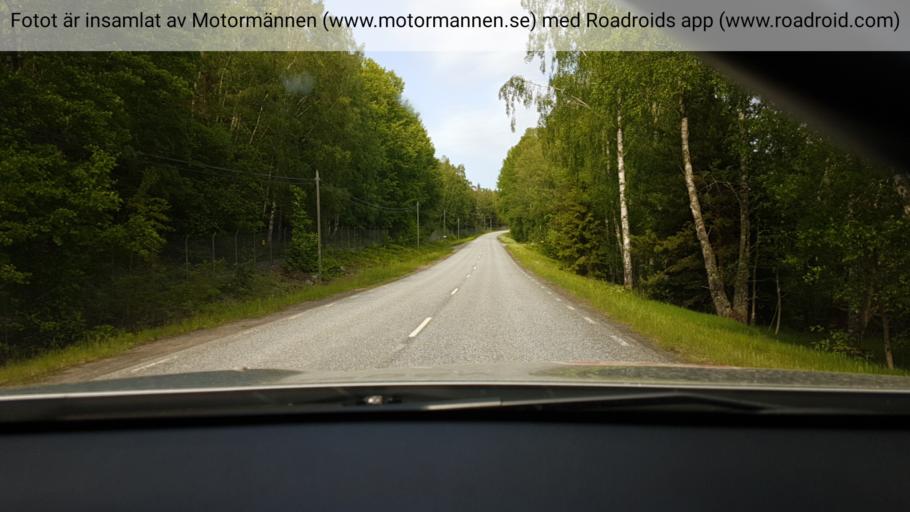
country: SE
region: Stockholm
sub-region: Nynashamns Kommun
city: Nynashamn
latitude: 58.9757
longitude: 18.0798
